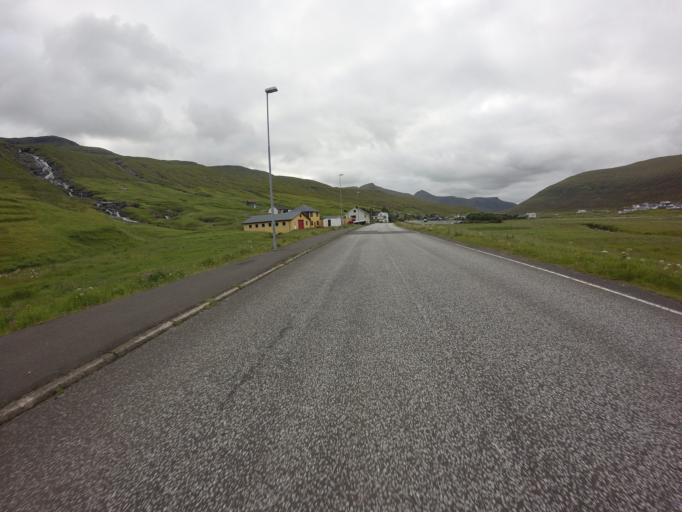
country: FO
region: Eysturoy
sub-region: Eidi
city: Eidi
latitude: 62.1855
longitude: -7.0289
